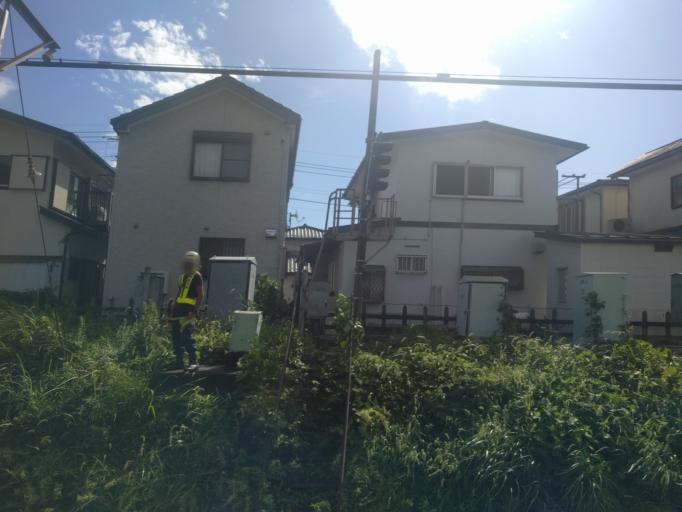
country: JP
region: Tokyo
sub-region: Machida-shi
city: Machida
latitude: 35.5546
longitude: 139.4613
